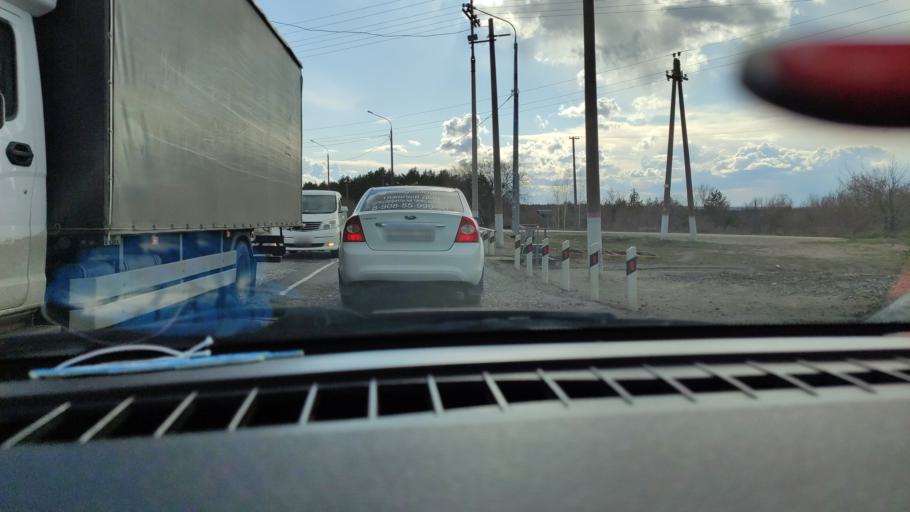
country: RU
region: Saratov
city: Sennoy
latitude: 52.1499
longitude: 46.9480
